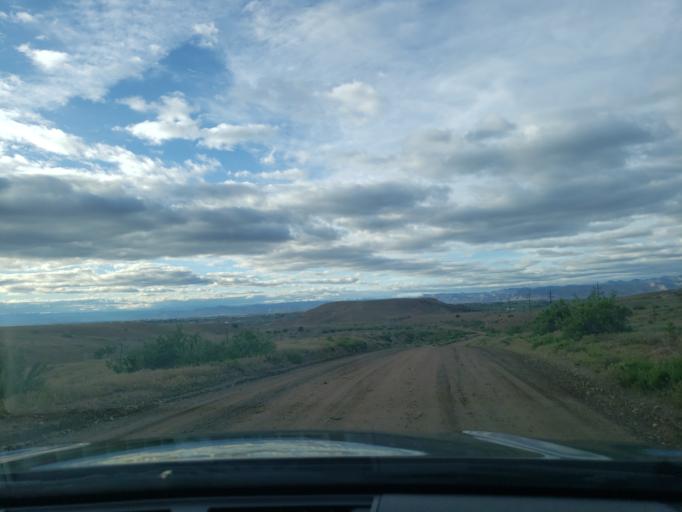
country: US
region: Colorado
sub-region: Mesa County
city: Fruita
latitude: 39.1429
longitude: -108.7586
